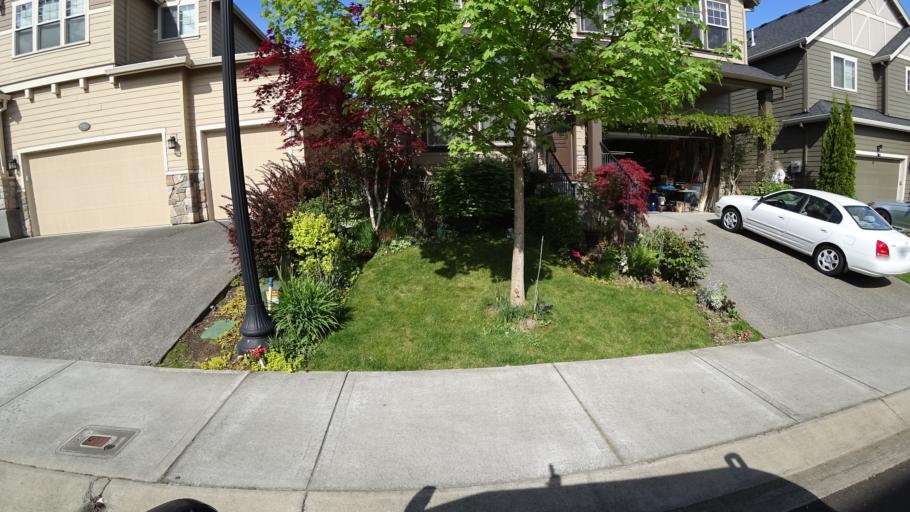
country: US
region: Oregon
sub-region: Washington County
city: Aloha
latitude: 45.4480
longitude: -122.8512
